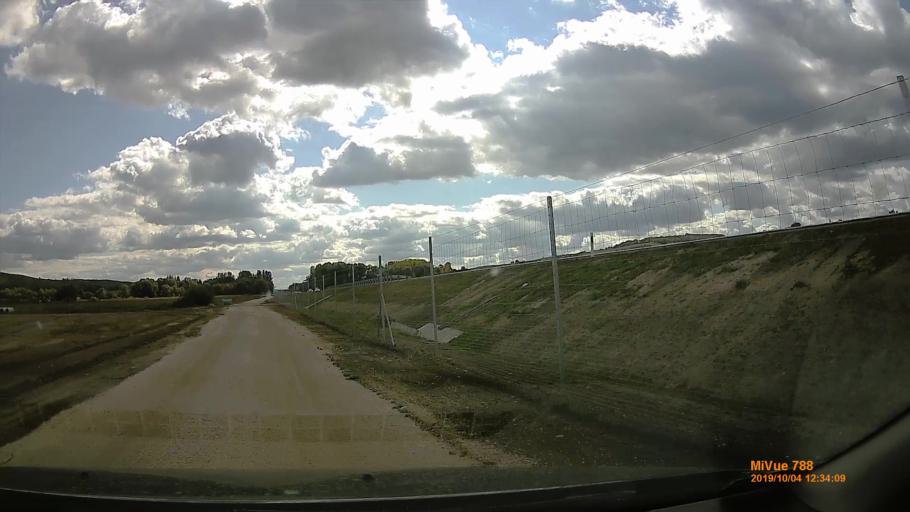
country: HU
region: Somogy
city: Karad
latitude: 46.6872
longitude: 17.7734
